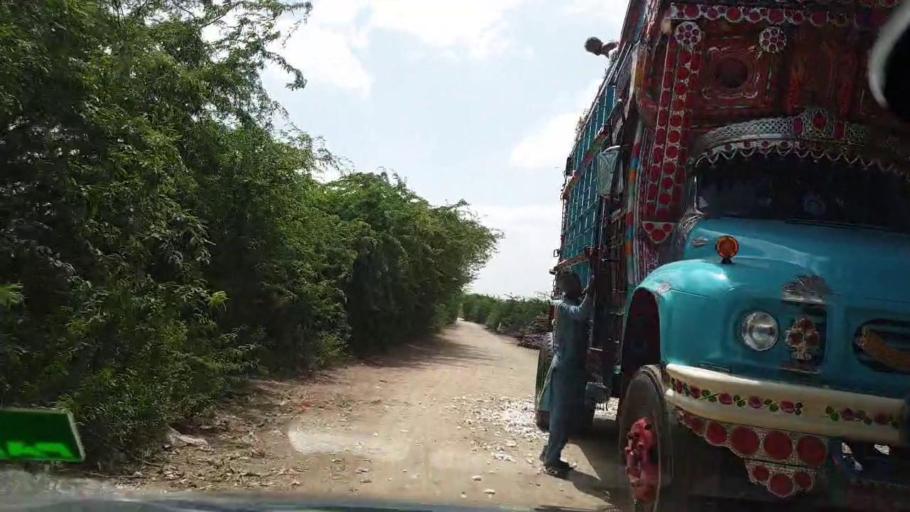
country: PK
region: Sindh
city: Kadhan
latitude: 24.5572
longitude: 69.2114
